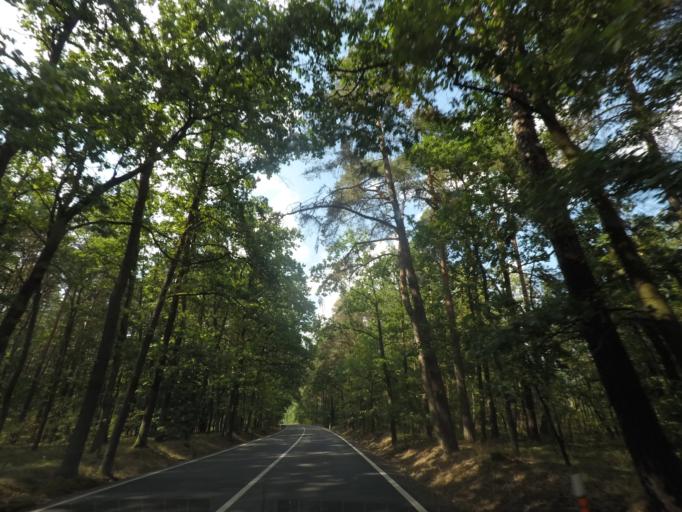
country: CZ
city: Borohradek
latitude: 50.1090
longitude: 16.0774
